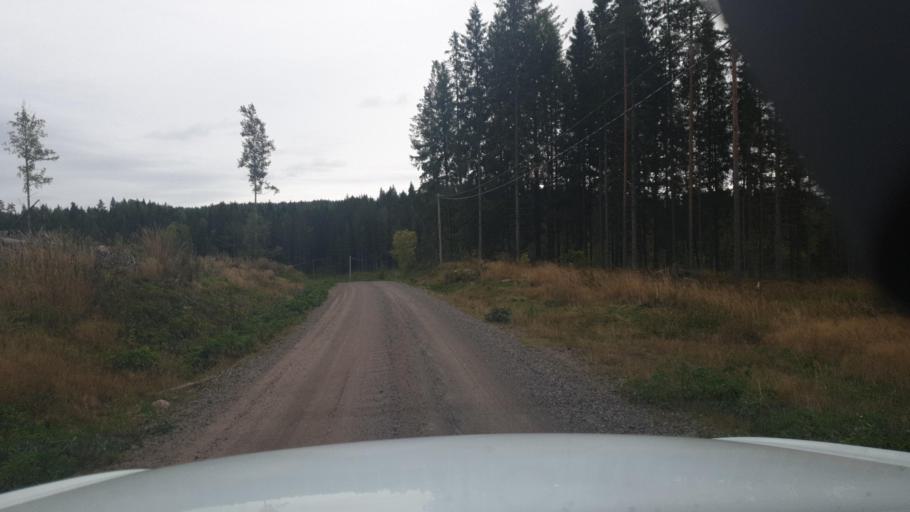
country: SE
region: Vaermland
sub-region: Eda Kommun
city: Charlottenberg
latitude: 60.1484
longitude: 12.5953
